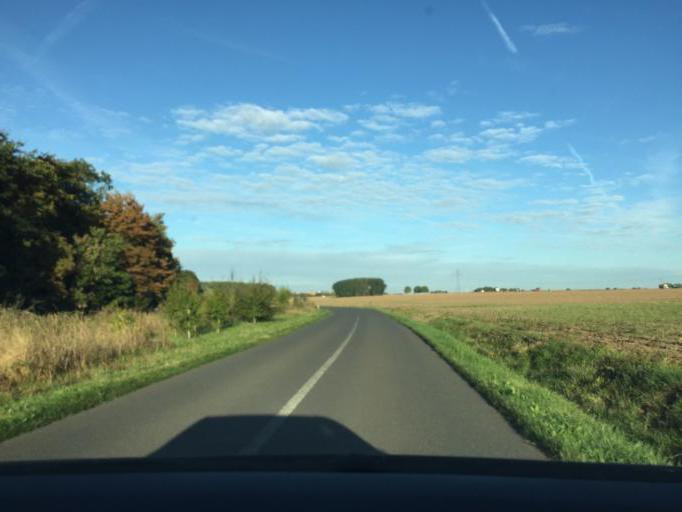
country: FR
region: Ile-de-France
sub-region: Departement de l'Essonne
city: Villiers-le-Bacle
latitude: 48.7254
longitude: 2.1375
